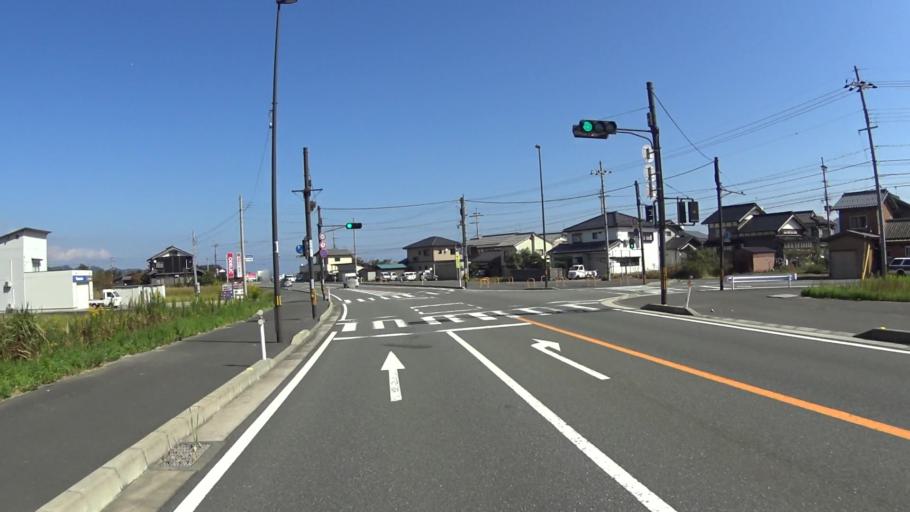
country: JP
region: Kyoto
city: Miyazu
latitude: 35.5881
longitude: 135.1918
